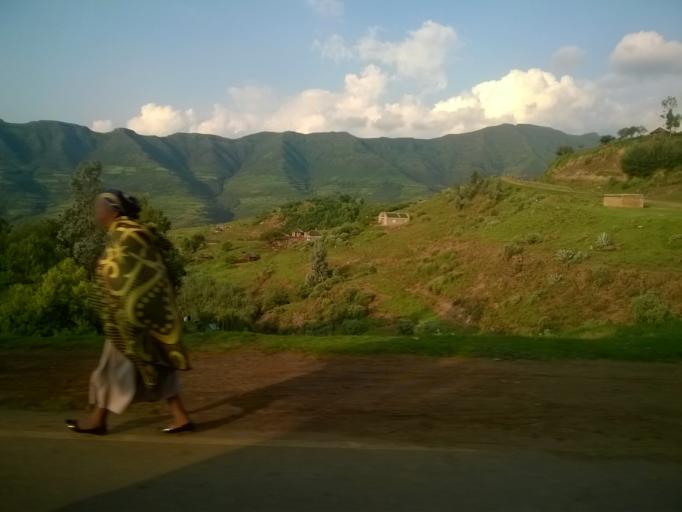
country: LS
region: Butha-Buthe
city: Butha-Buthe
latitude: -29.0367
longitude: 28.2918
